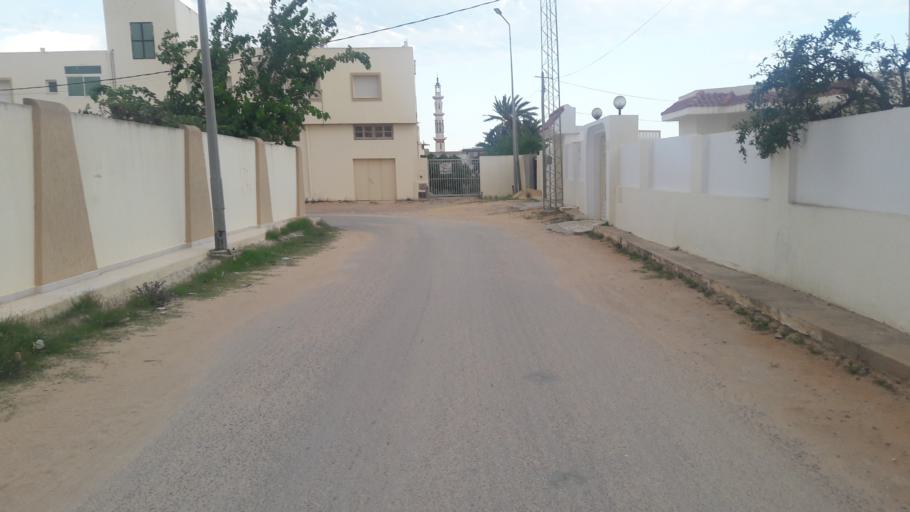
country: TN
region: Safaqis
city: Al Qarmadah
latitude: 34.8101
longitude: 10.7478
